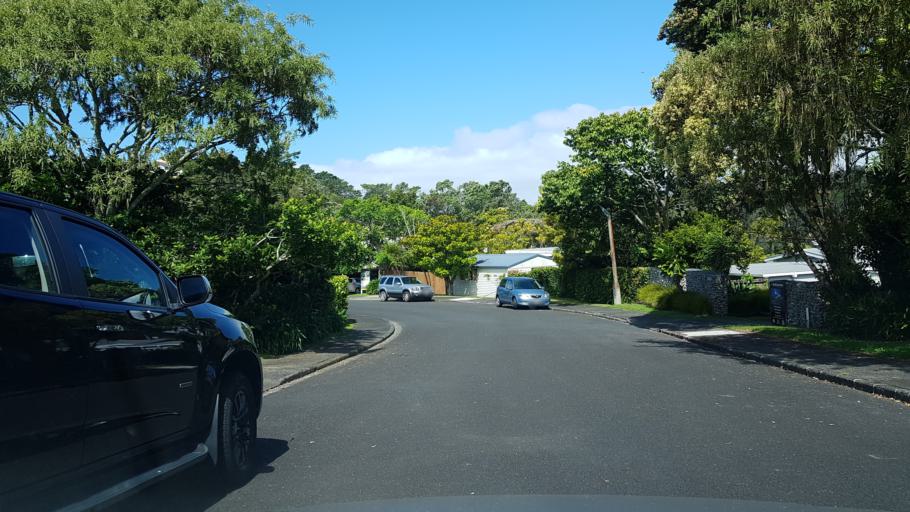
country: NZ
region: Auckland
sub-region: Auckland
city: North Shore
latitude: -36.8122
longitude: 174.6913
